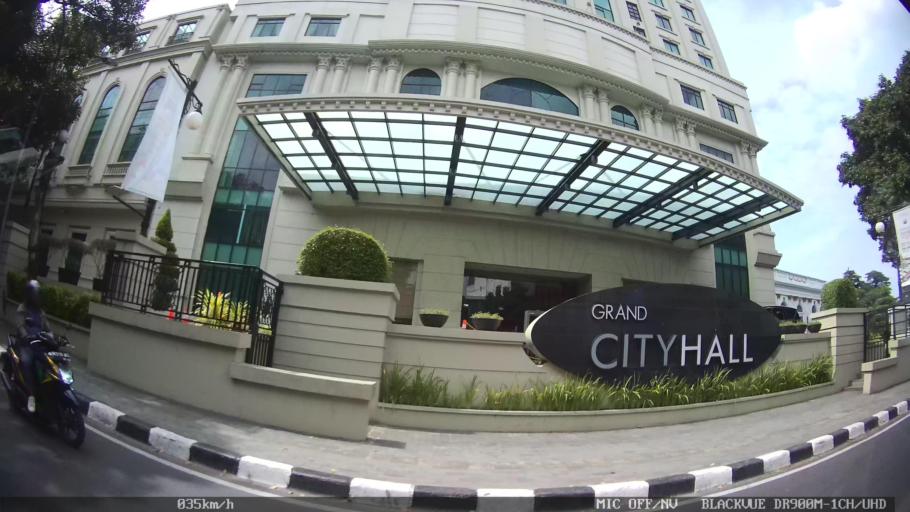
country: ID
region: North Sumatra
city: Medan
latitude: 3.5900
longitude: 98.6758
